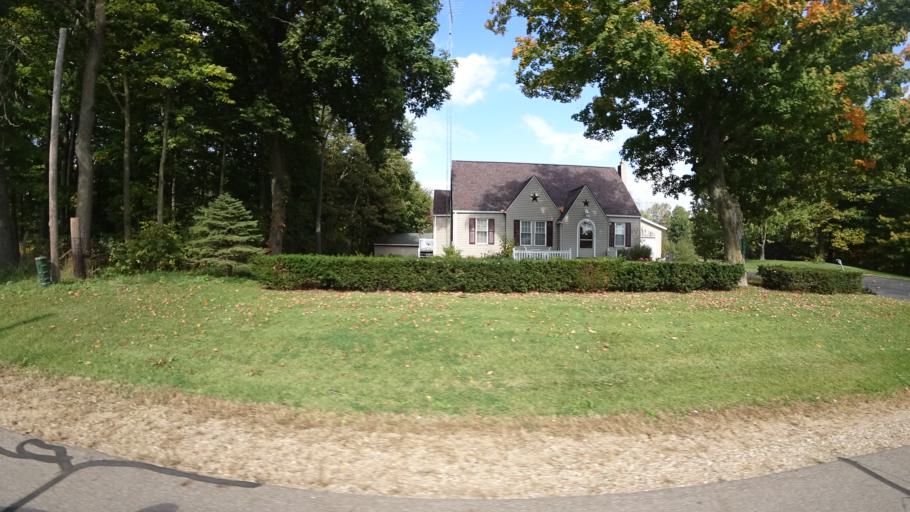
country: US
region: Michigan
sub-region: Saint Joseph County
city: Three Rivers
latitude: 41.9256
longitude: -85.6147
